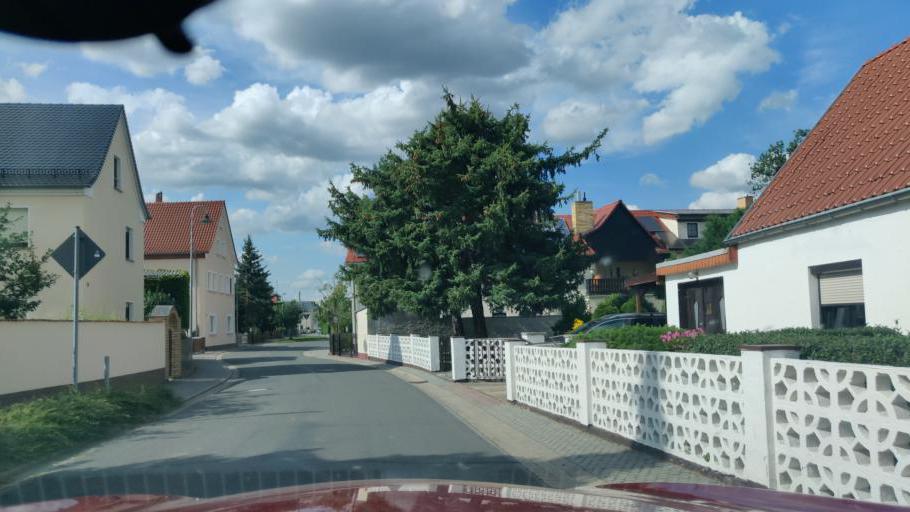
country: DE
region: Saxony
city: Schildau
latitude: 51.4832
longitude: 12.9046
